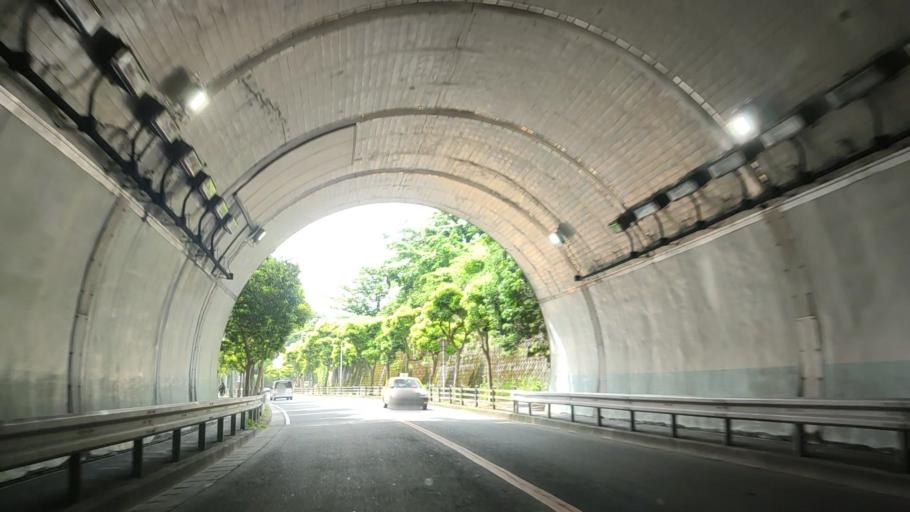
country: JP
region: Kanagawa
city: Yokohama
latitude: 35.3987
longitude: 139.6091
